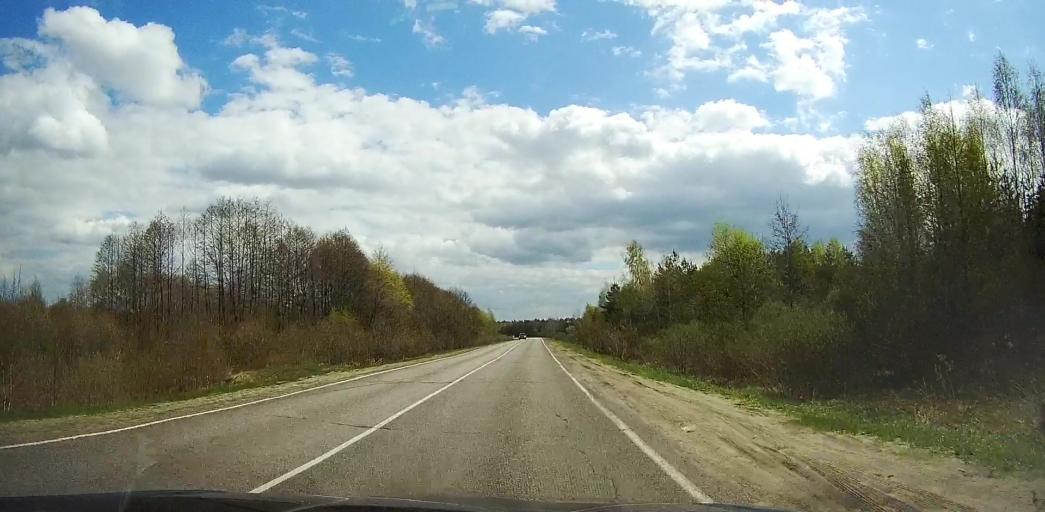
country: RU
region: Moskovskaya
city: Davydovo
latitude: 55.5489
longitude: 38.8068
